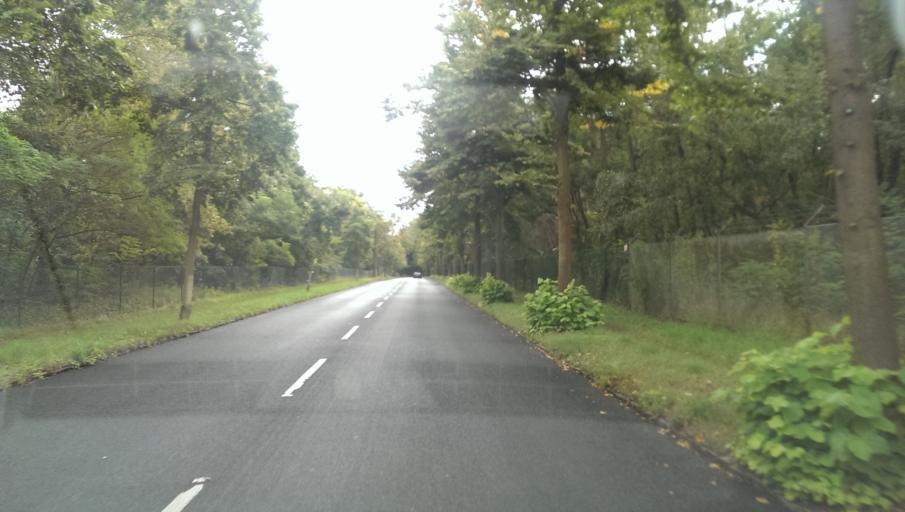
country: DE
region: Berlin
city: Haselhorst
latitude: 52.5230
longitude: 13.2187
